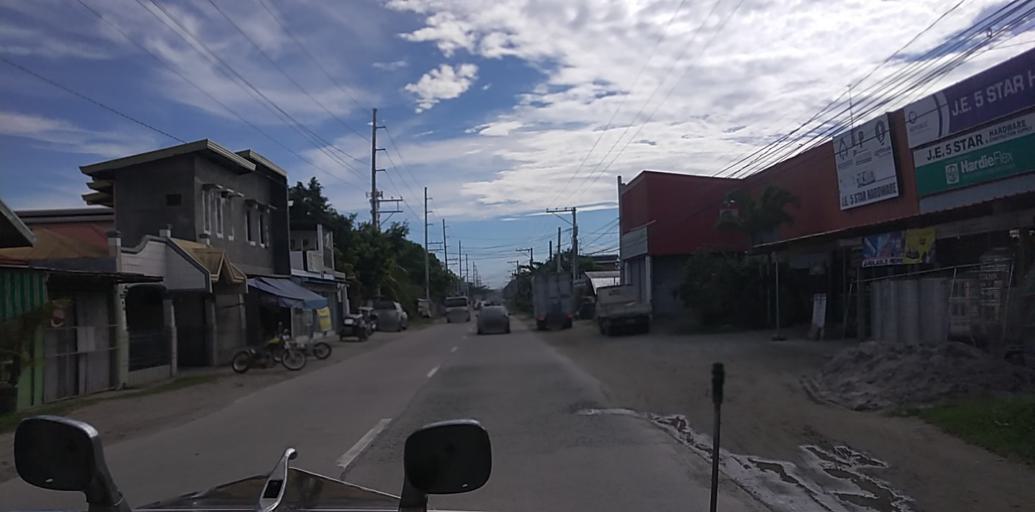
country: PH
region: Central Luzon
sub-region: Province of Pampanga
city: Arayat
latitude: 15.1479
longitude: 120.7597
